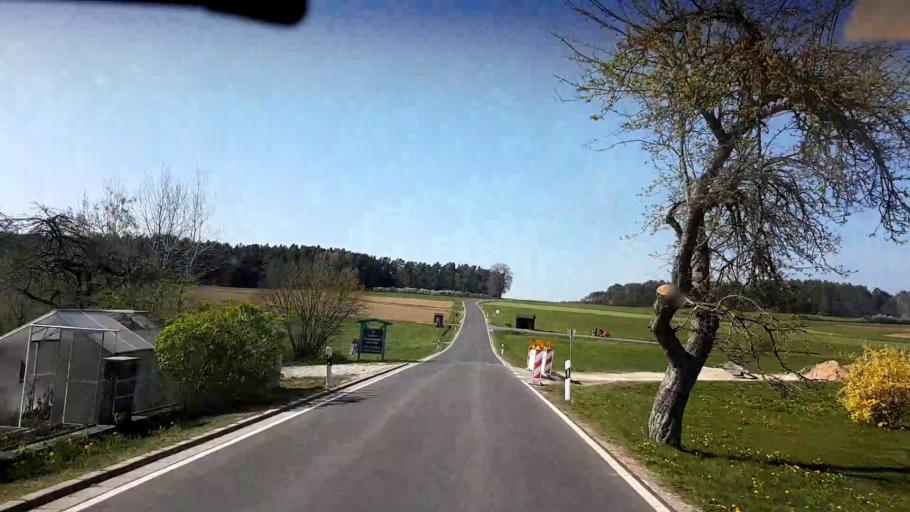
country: DE
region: Bavaria
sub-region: Upper Franconia
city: Pottenstein
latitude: 49.7985
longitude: 11.3765
